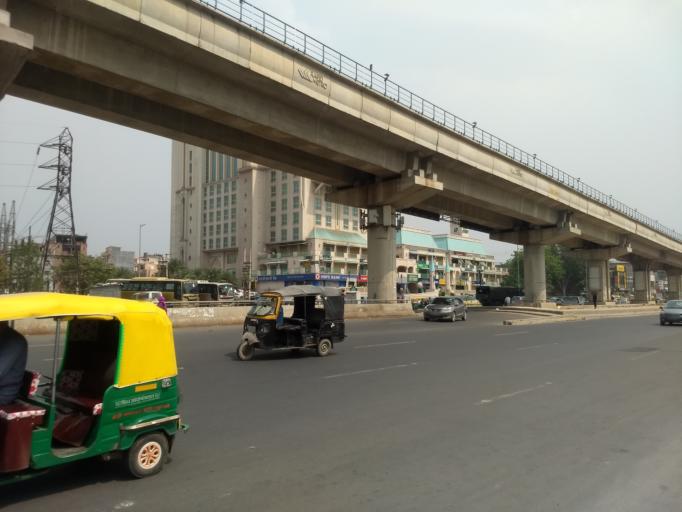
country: IN
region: Haryana
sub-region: Gurgaon
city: Gurgaon
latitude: 28.4839
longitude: 77.0948
